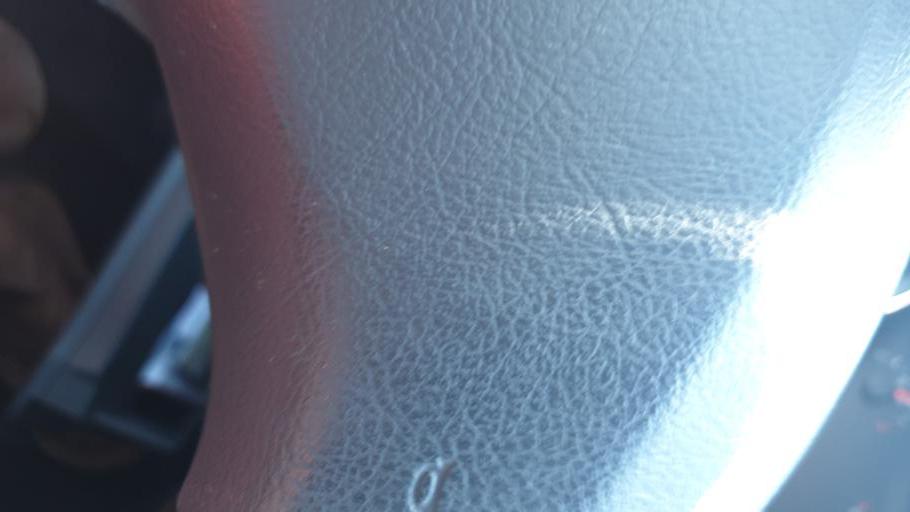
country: IL
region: Haifa
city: Qiryat Ata
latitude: 32.8135
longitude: 35.0964
